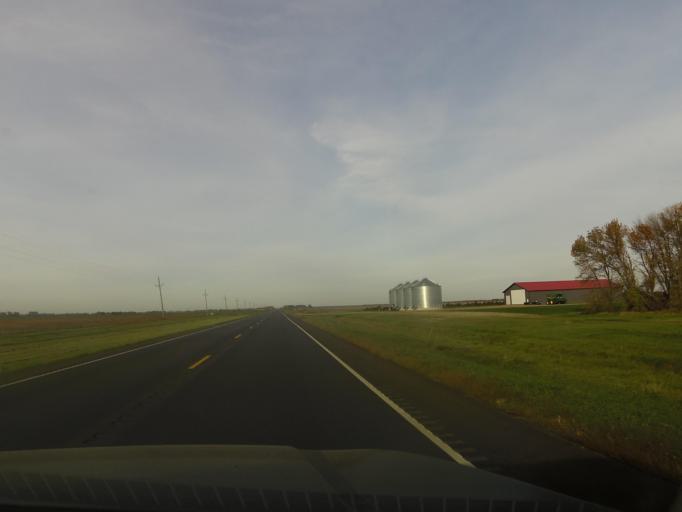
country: US
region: North Dakota
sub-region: Pembina County
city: Cavalier
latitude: 48.8044
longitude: -97.5034
